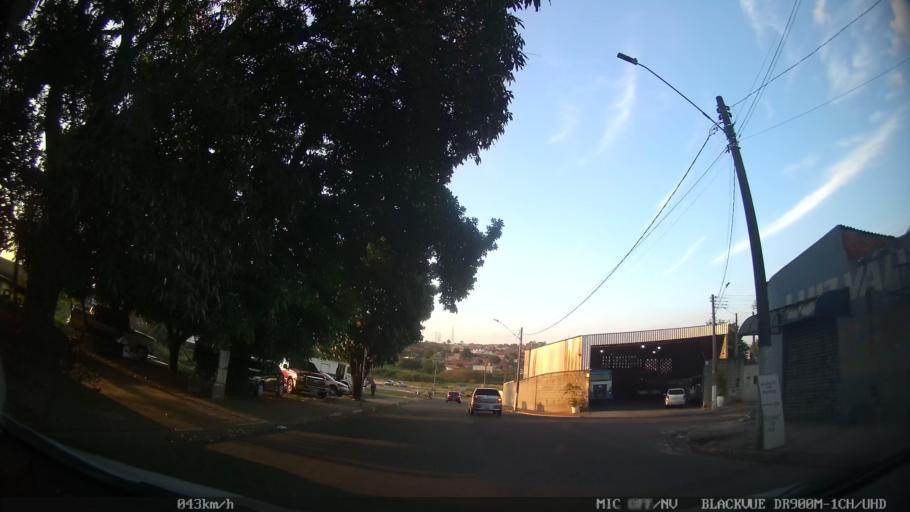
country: BR
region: Sao Paulo
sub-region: Hortolandia
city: Hortolandia
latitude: -22.8688
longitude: -47.2003
